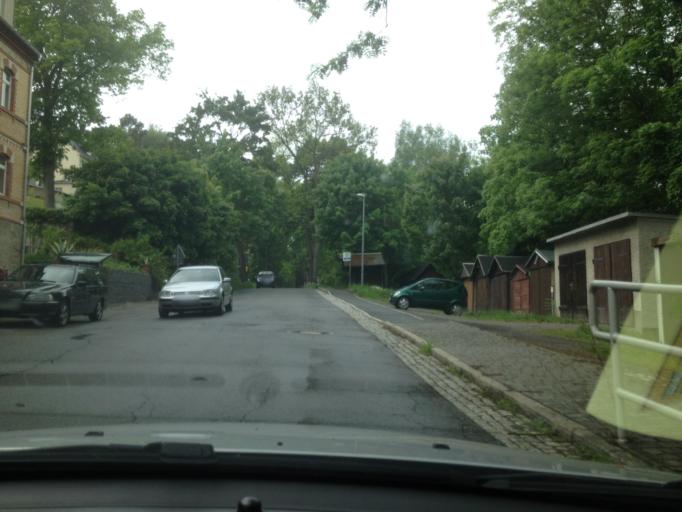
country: DE
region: Saxony
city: Annaberg-Buchholz
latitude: 50.5550
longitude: 12.9987
